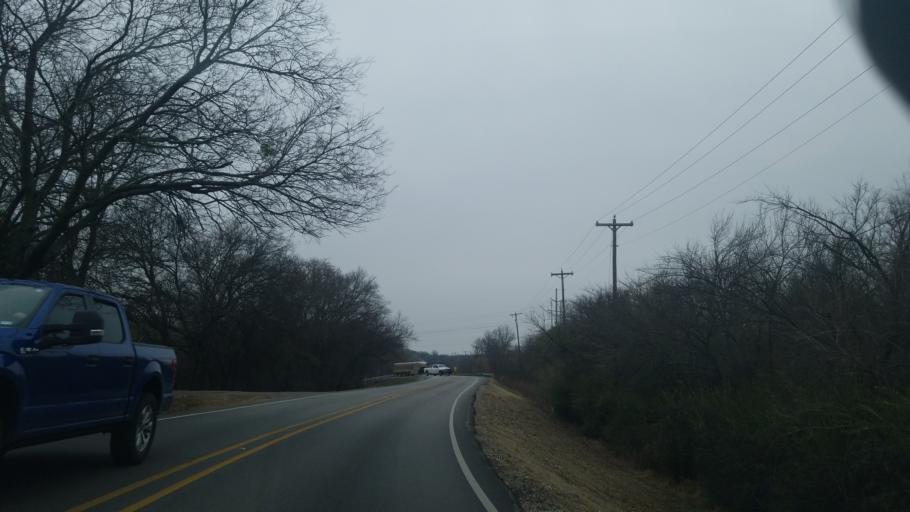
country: US
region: Texas
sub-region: Denton County
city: Argyle
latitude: 33.1534
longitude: -97.1418
